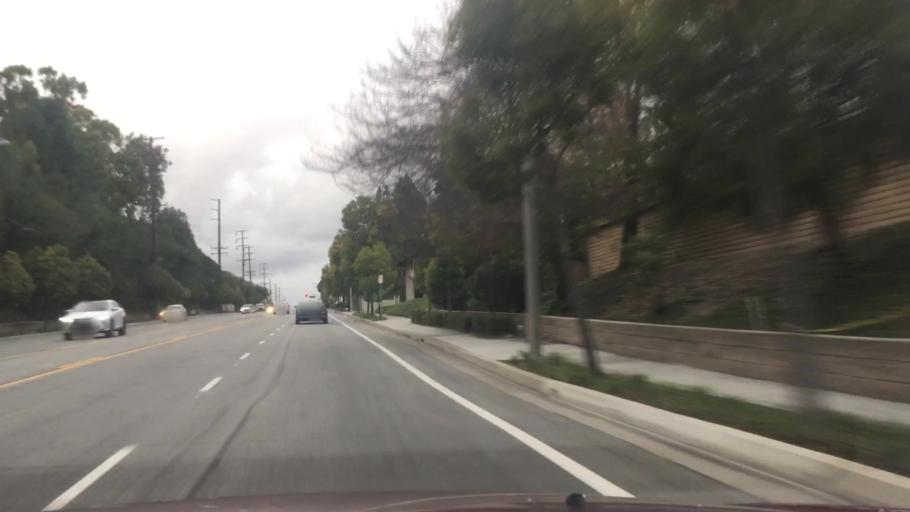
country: US
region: California
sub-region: Los Angeles County
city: East La Mirada
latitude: 33.9075
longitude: -117.9942
